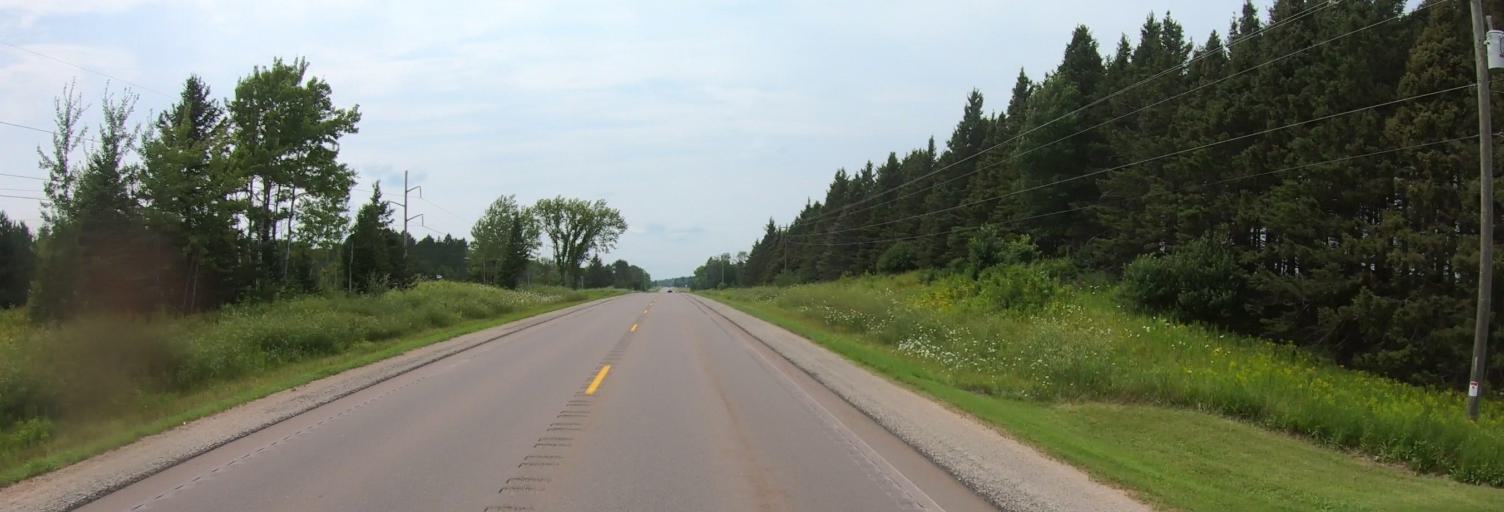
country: US
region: Michigan
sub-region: Alger County
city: Munising
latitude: 46.3517
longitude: -87.0138
